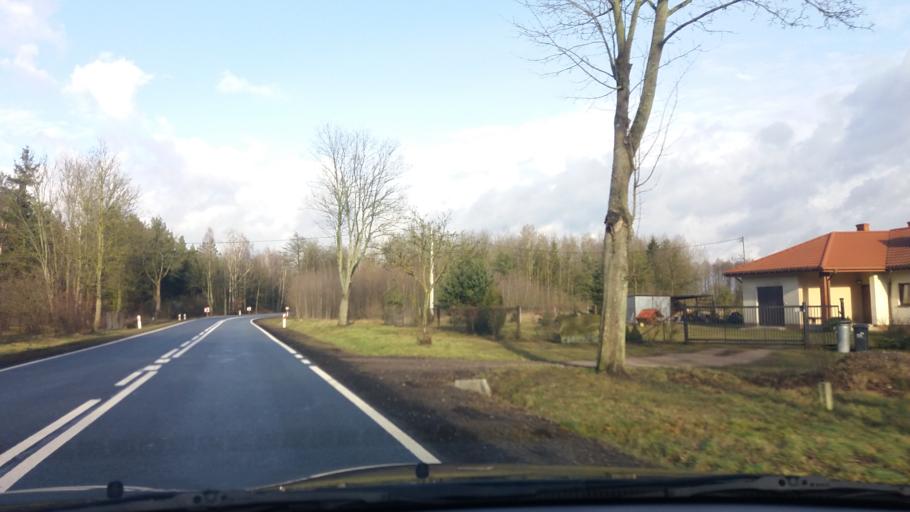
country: PL
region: Masovian Voivodeship
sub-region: Powiat przasnyski
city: Chorzele
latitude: 53.2838
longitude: 20.9020
